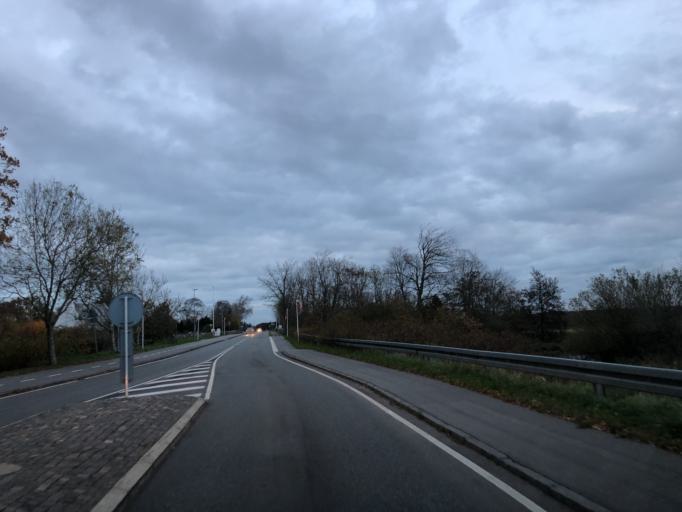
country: DK
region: Central Jutland
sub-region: Holstebro Kommune
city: Ulfborg
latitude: 56.3426
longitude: 8.3517
